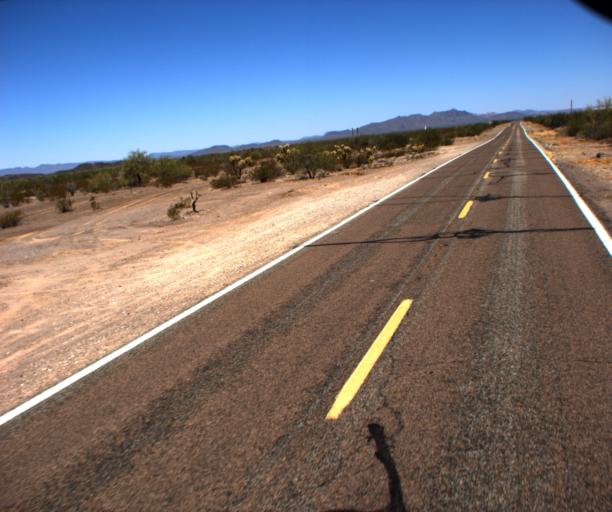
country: US
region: Arizona
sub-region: Pima County
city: Ajo
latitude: 32.2313
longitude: -112.7131
